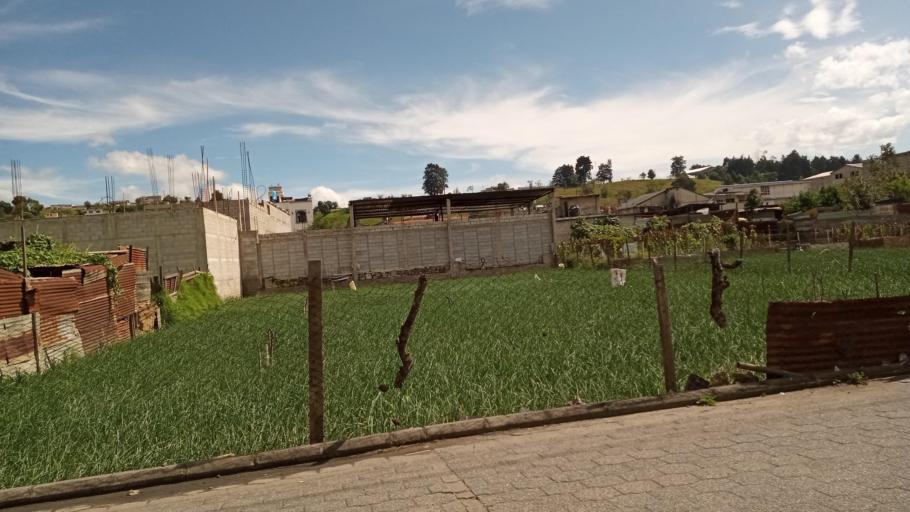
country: GT
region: Quetzaltenango
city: Quetzaltenango
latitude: 14.8449
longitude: -91.5098
